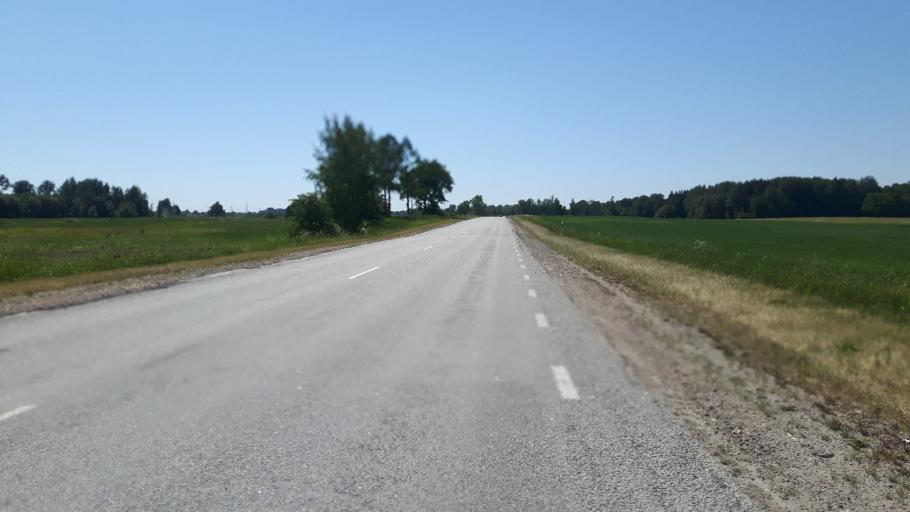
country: EE
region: Paernumaa
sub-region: Sindi linn
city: Sindi
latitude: 58.4460
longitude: 24.7630
